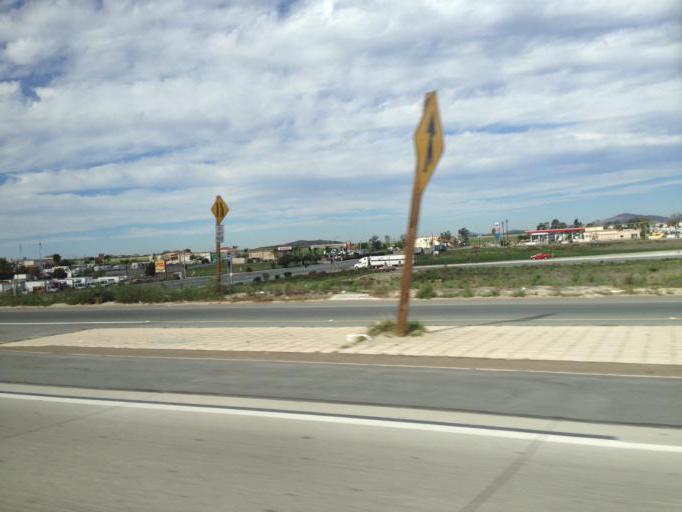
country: MX
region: Baja California
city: Tijuana
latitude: 32.5643
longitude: -116.9610
